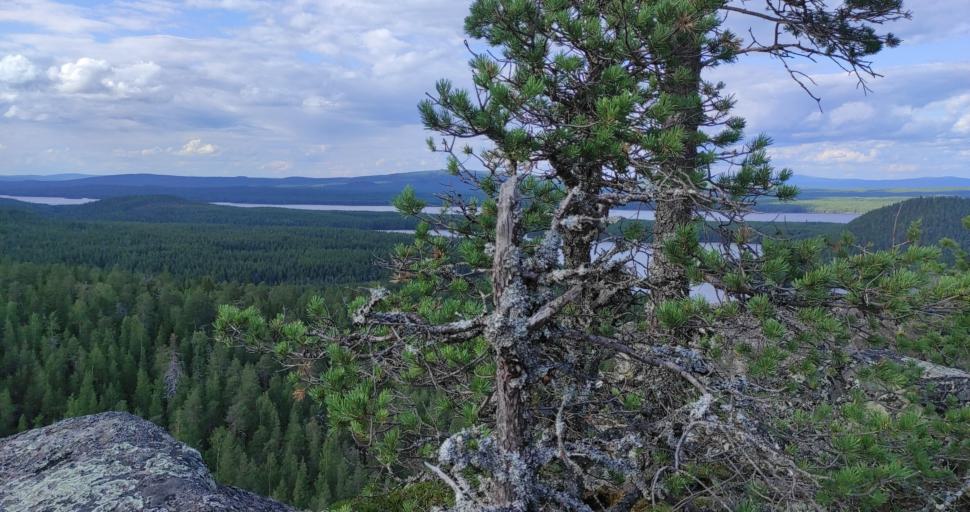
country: RU
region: Murmansk
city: Zelenoborskiy
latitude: 66.6962
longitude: 32.4722
